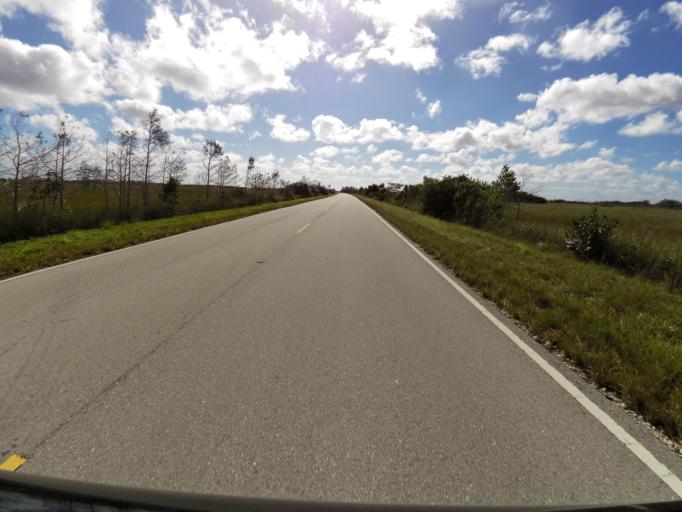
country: US
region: Florida
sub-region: Miami-Dade County
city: Florida City
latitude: 25.3747
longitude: -80.8148
